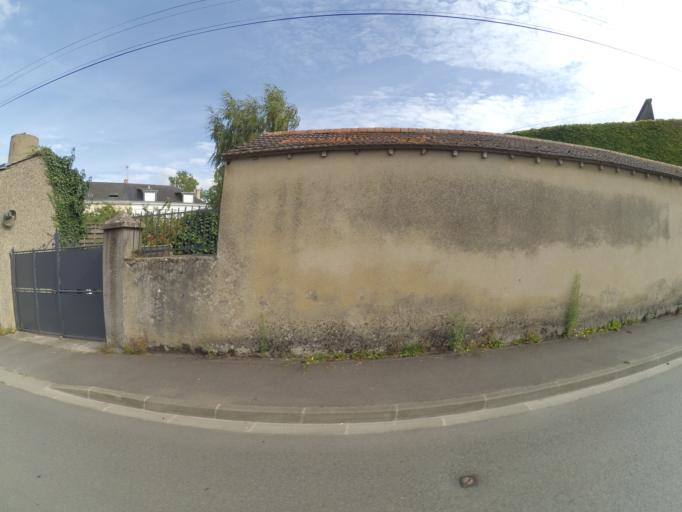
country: FR
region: Pays de la Loire
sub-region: Departement de Maine-et-Loire
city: Doue-la-Fontaine
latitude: 47.1901
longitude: -0.2775
